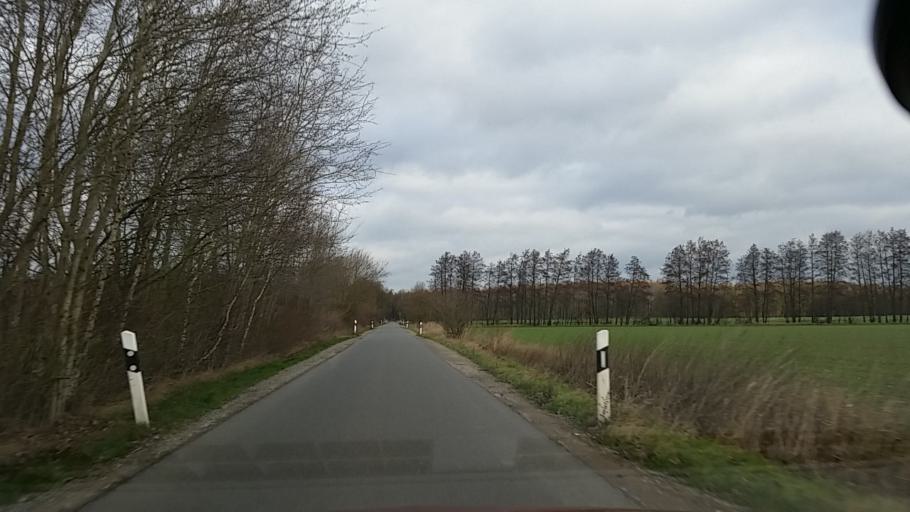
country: DE
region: Lower Saxony
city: Luder
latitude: 52.7644
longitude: 10.6659
